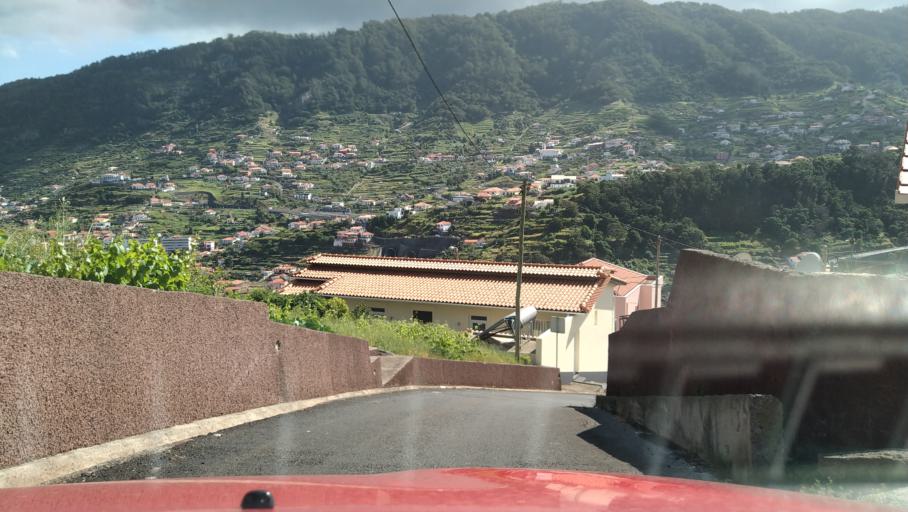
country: PT
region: Madeira
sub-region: Machico
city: Machico
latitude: 32.7356
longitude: -16.7754
